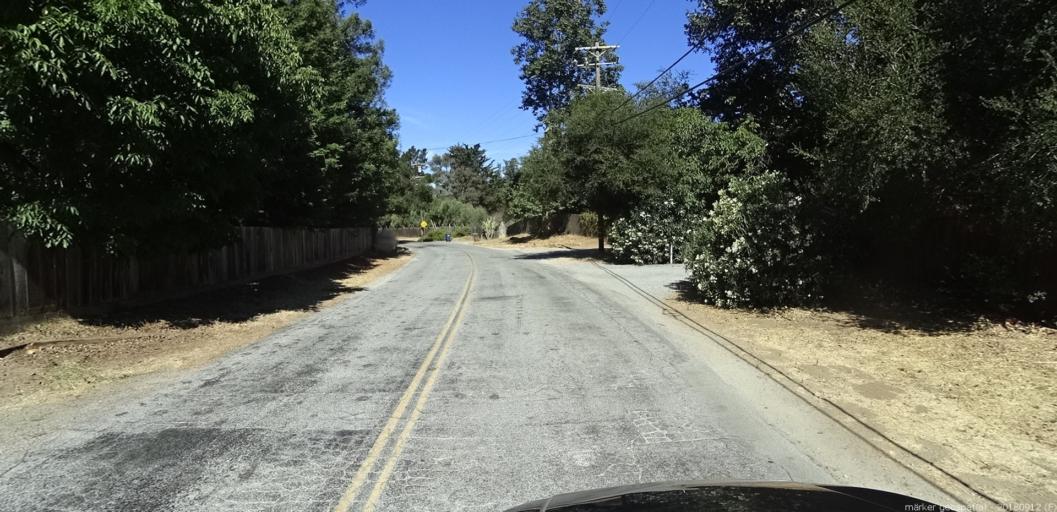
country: US
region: California
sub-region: Monterey County
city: Carmel Valley Village
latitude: 36.4915
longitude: -121.7479
